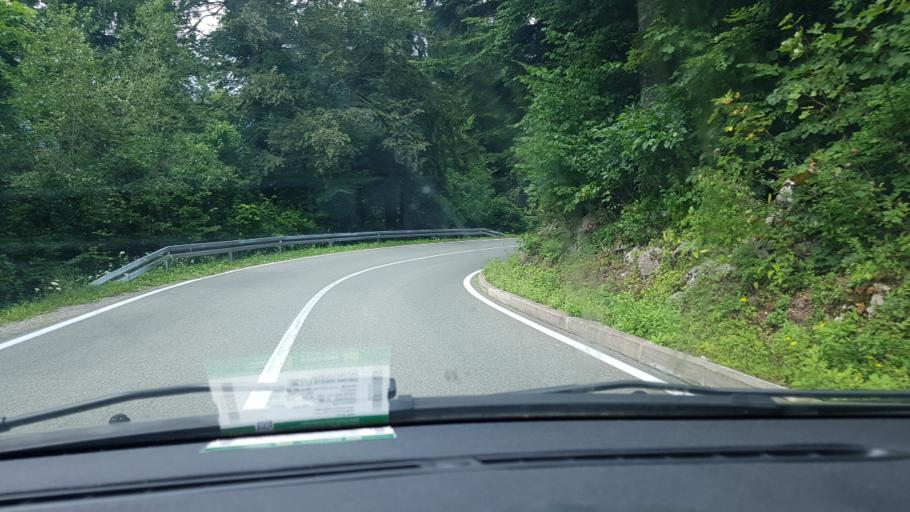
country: HR
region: Primorsko-Goranska
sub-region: Grad Delnice
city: Delnice
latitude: 45.3460
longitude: 14.7585
